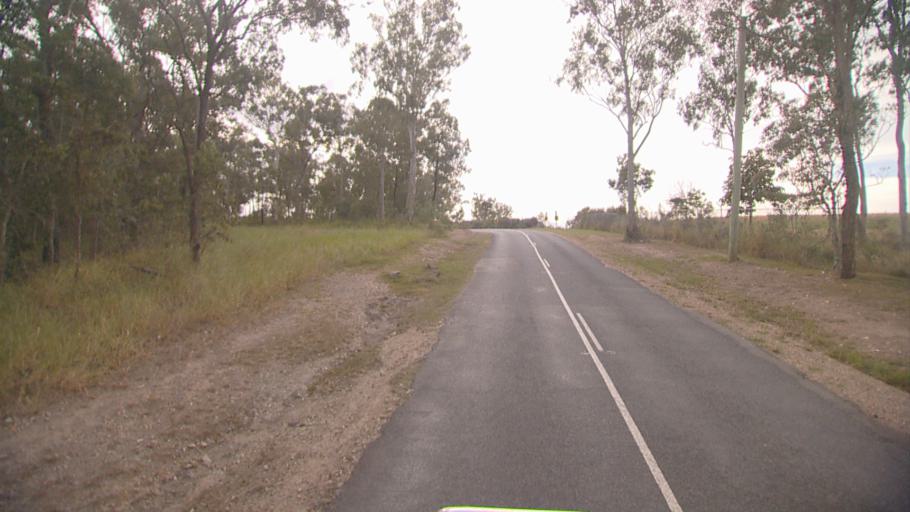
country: AU
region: Queensland
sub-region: Logan
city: Beenleigh
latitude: -27.7170
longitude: 153.1738
